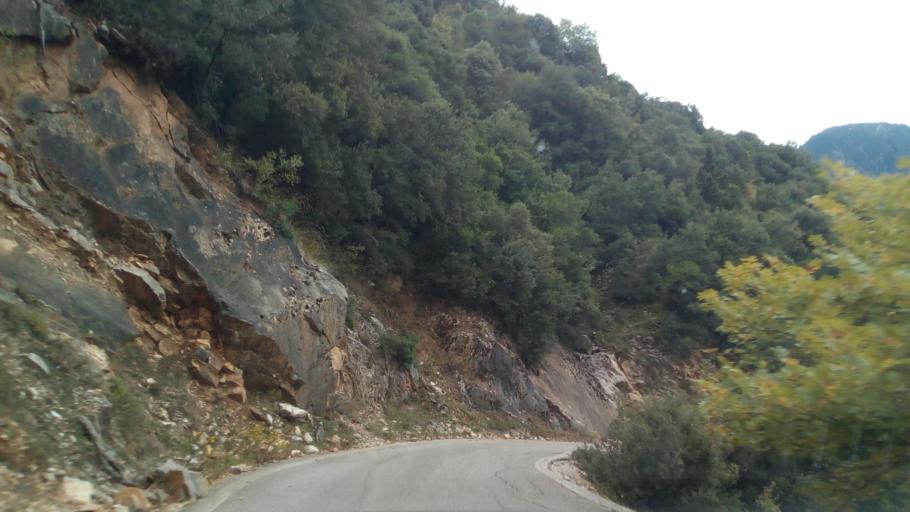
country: GR
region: West Greece
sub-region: Nomos Aitolias kai Akarnanias
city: Thermo
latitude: 38.6017
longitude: 21.8434
